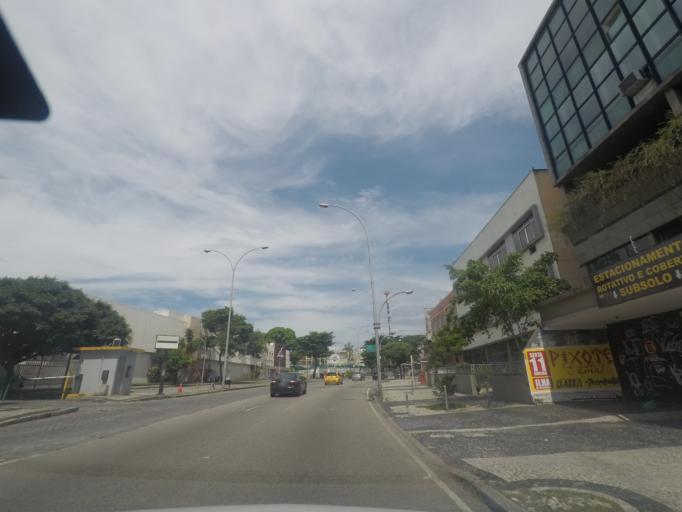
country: BR
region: Rio de Janeiro
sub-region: Rio De Janeiro
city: Rio de Janeiro
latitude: -22.8042
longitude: -43.2042
